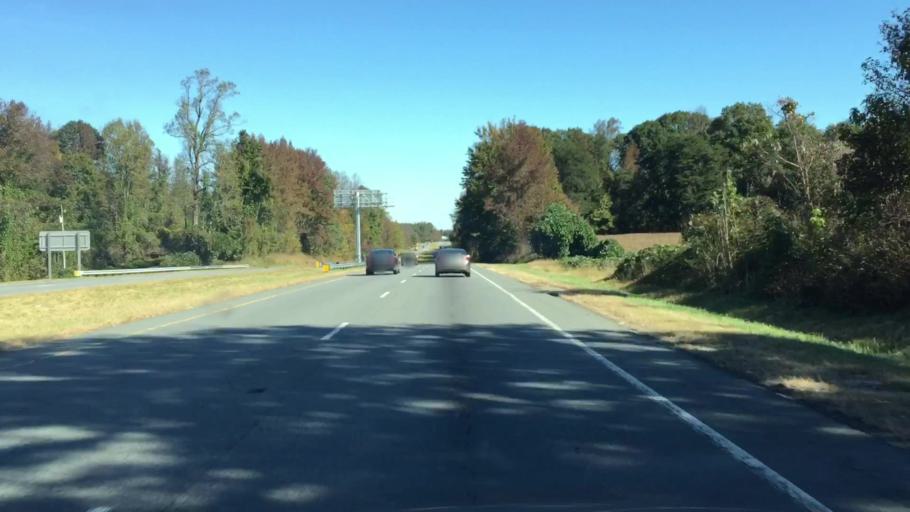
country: US
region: North Carolina
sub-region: Rockingham County
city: Reidsville
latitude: 36.2333
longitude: -79.6747
